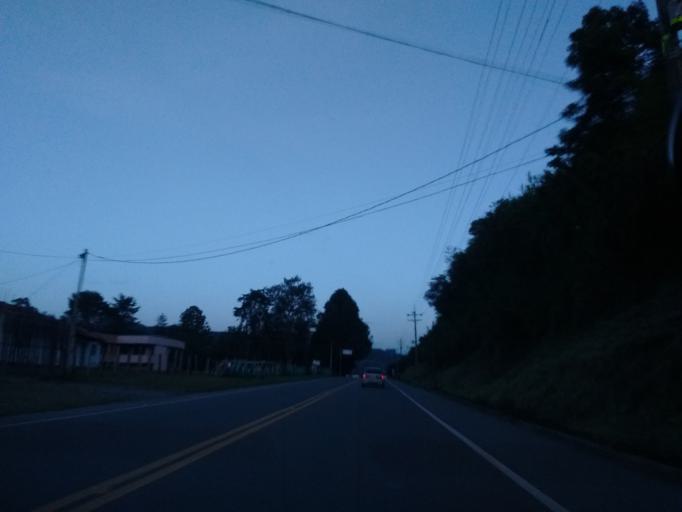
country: CO
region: Antioquia
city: Santuario
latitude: 6.1307
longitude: -75.2575
